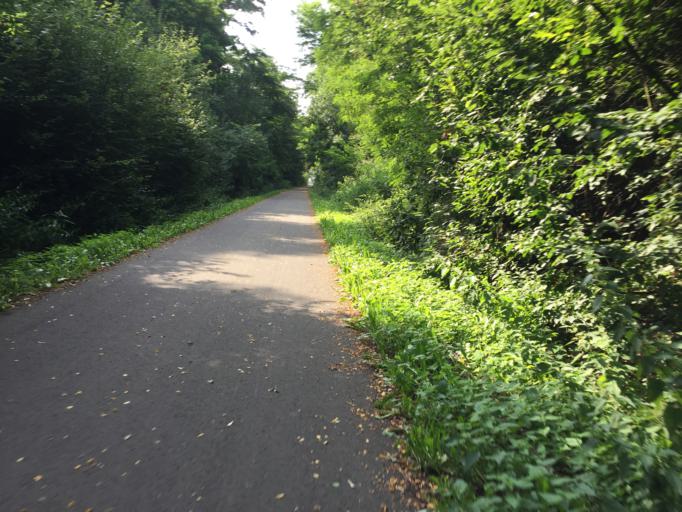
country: DE
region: Hesse
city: Schwalmstadt
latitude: 50.9083
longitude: 9.2091
